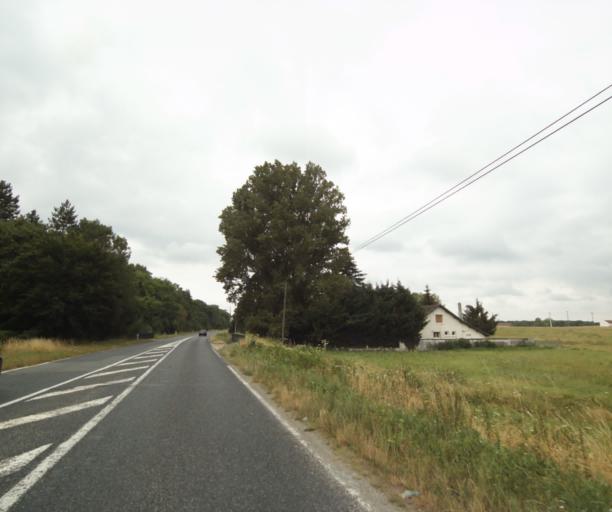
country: FR
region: Centre
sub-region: Departement du Loiret
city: Marigny-les-Usages
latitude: 47.9493
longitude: 2.0215
